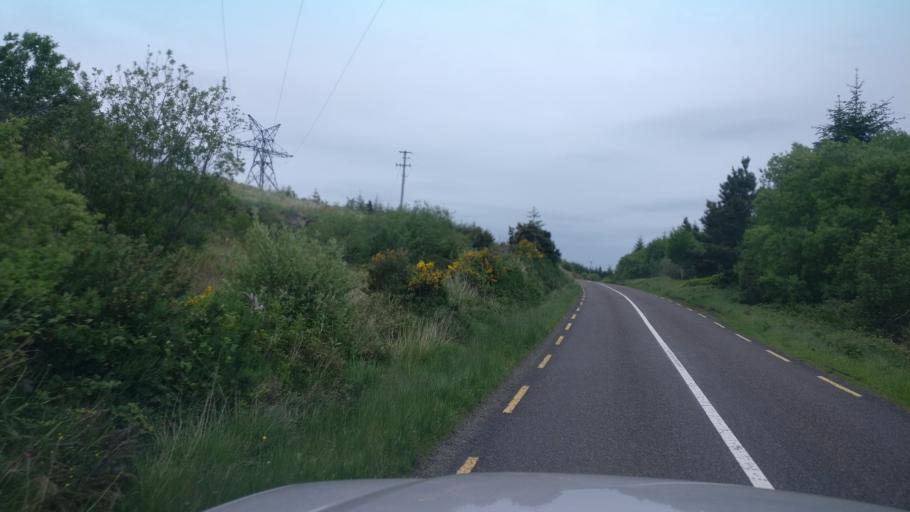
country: IE
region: Connaught
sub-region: County Galway
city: Loughrea
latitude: 53.0730
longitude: -8.5769
